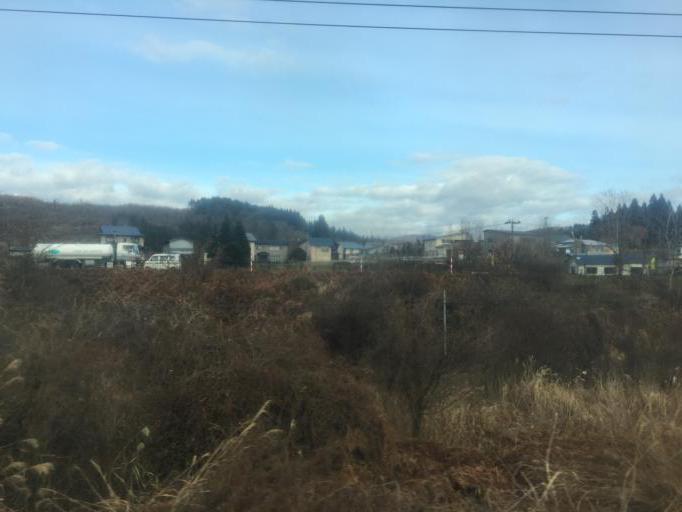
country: JP
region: Akita
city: Takanosu
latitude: 40.2639
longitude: 140.4207
